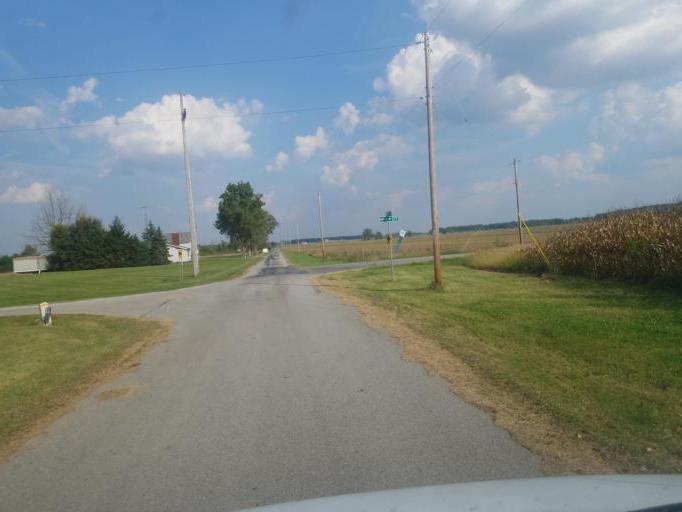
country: US
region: Ohio
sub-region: Hancock County
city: Arlington
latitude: 40.8194
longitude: -83.6338
